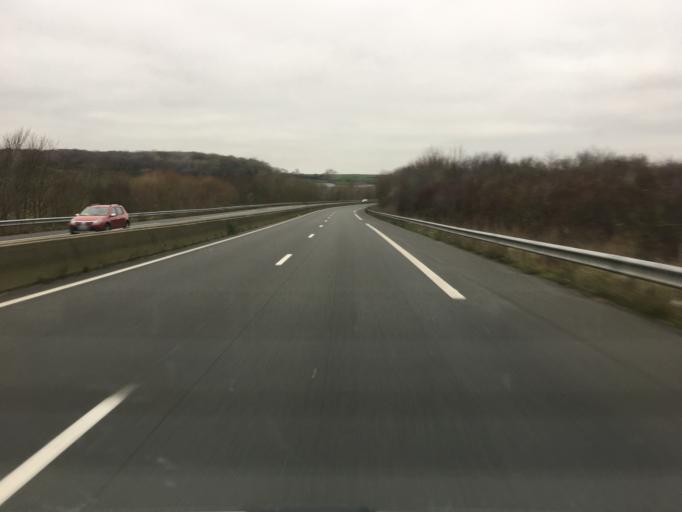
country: FR
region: Nord-Pas-de-Calais
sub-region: Departement du Pas-de-Calais
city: Wimille
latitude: 50.7781
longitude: 1.6555
